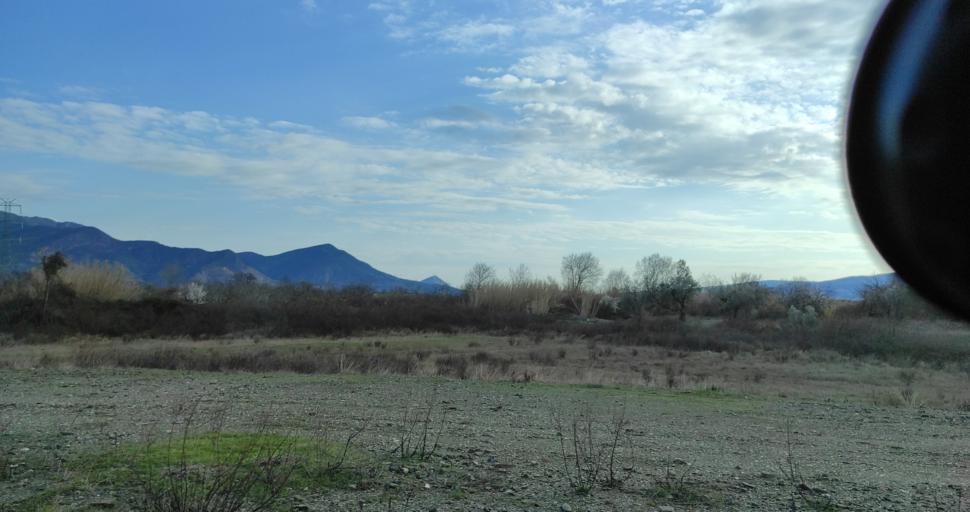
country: AL
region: Lezhe
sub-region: Rrethi i Lezhes
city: Kallmeti i Madh
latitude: 41.8792
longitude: 19.6661
